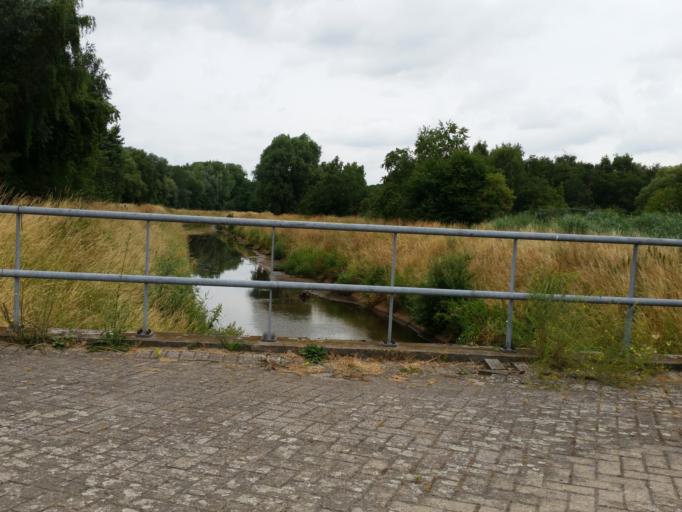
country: BE
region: Flanders
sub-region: Provincie Antwerpen
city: Mechelen
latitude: 51.0371
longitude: 4.5050
